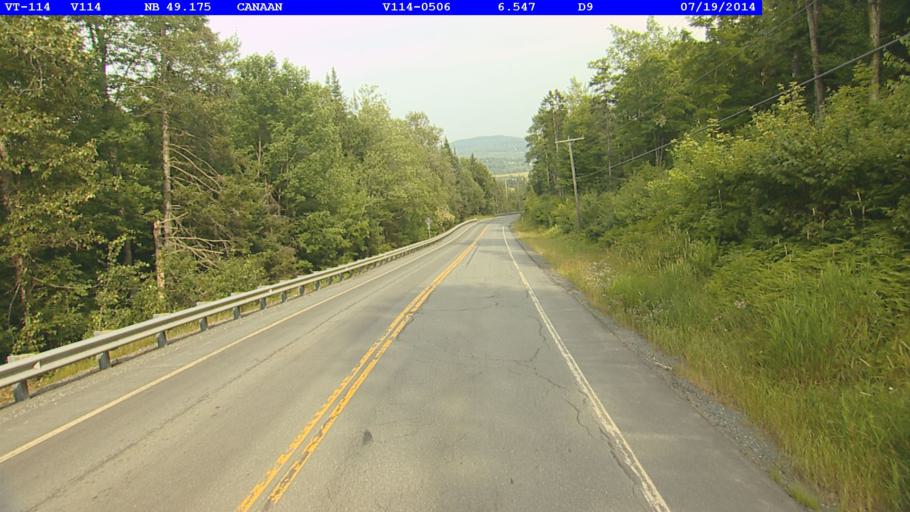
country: US
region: New Hampshire
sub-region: Coos County
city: Colebrook
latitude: 45.0096
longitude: -71.5650
